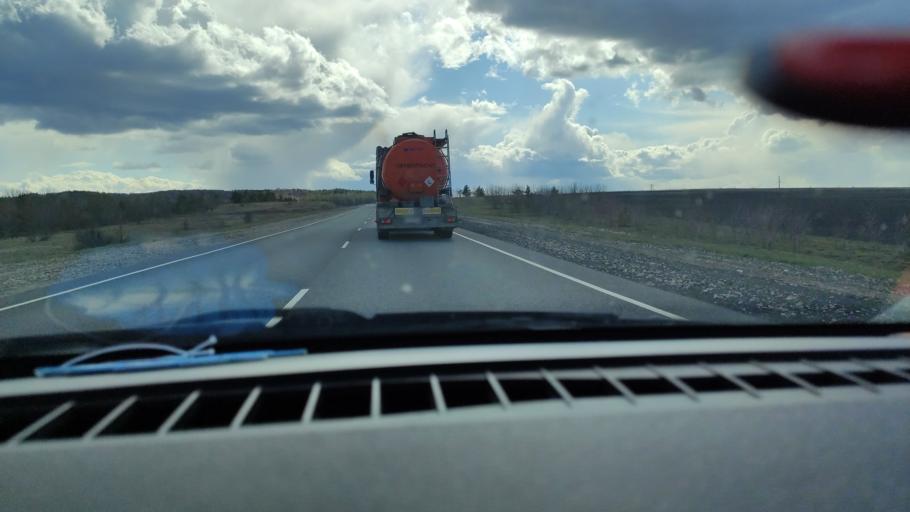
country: RU
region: Saratov
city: Khvalynsk
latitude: 52.5498
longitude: 48.0732
